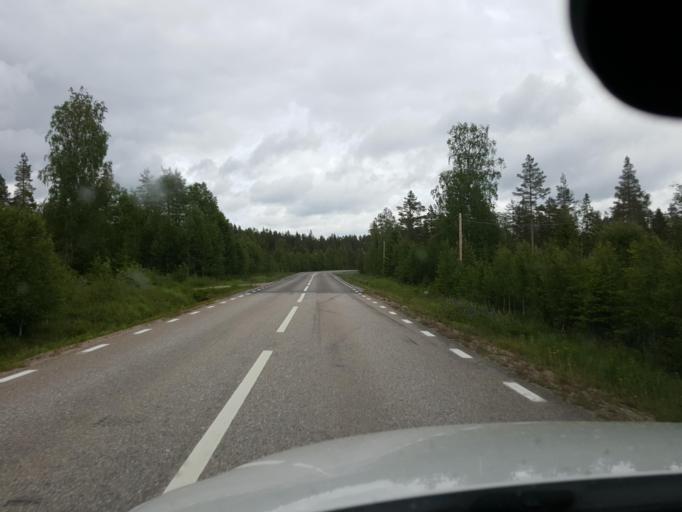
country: SE
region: Gaevleborg
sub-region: Ljusdals Kommun
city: Farila
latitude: 61.7612
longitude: 15.4877
